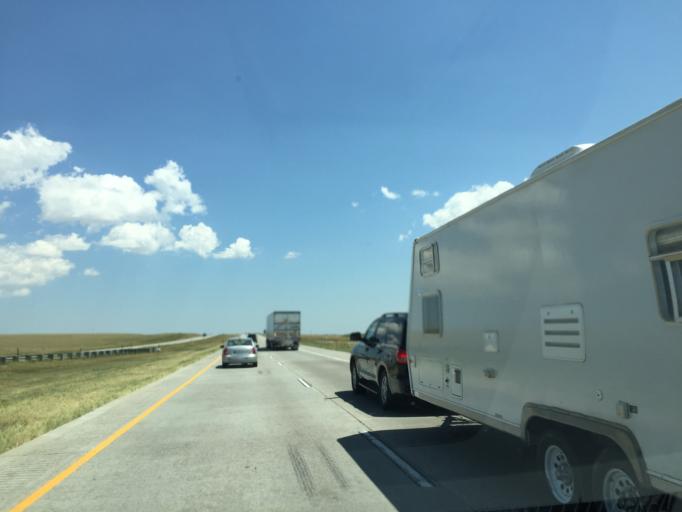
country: US
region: Colorado
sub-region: Lincoln County
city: Limon
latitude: 39.2839
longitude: -103.7789
